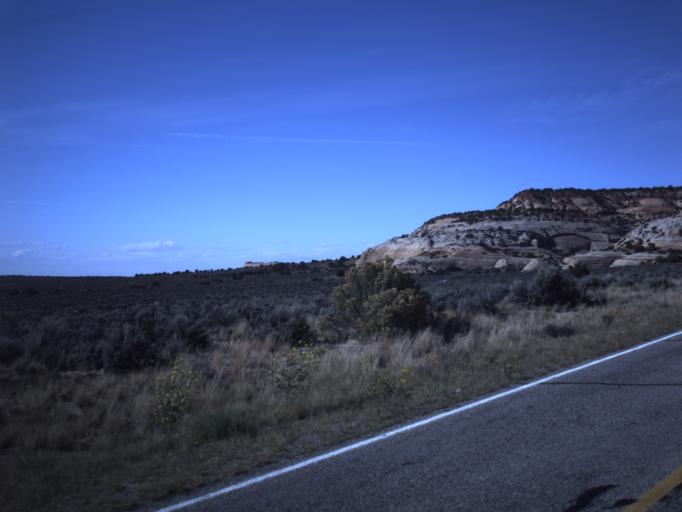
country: US
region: Utah
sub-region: San Juan County
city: Monticello
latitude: 38.0568
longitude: -109.4081
